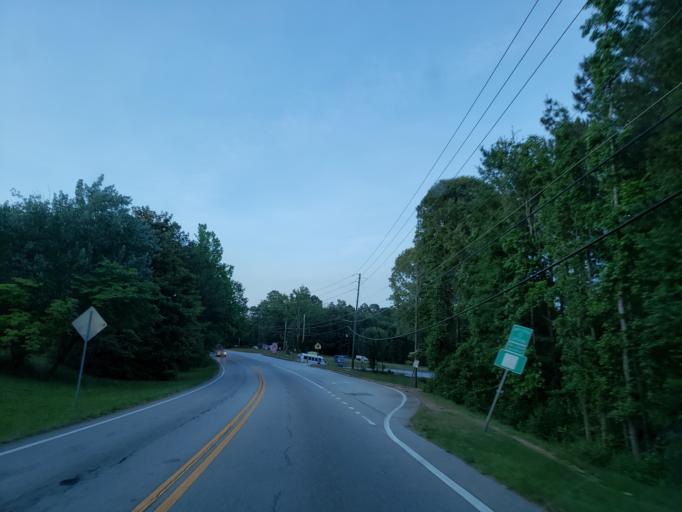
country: US
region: Georgia
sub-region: Douglas County
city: Douglasville
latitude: 33.6815
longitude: -84.8036
